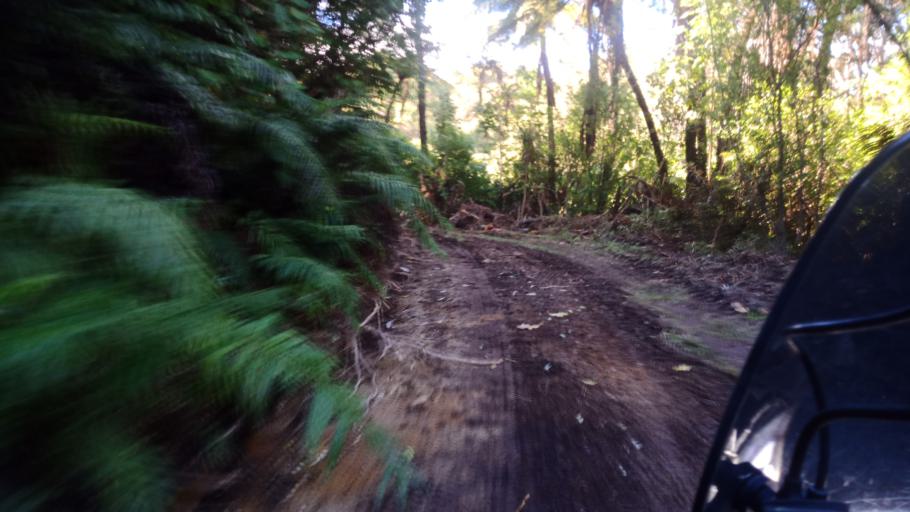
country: NZ
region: Hawke's Bay
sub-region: Wairoa District
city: Wairoa
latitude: -39.0011
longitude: 177.0598
